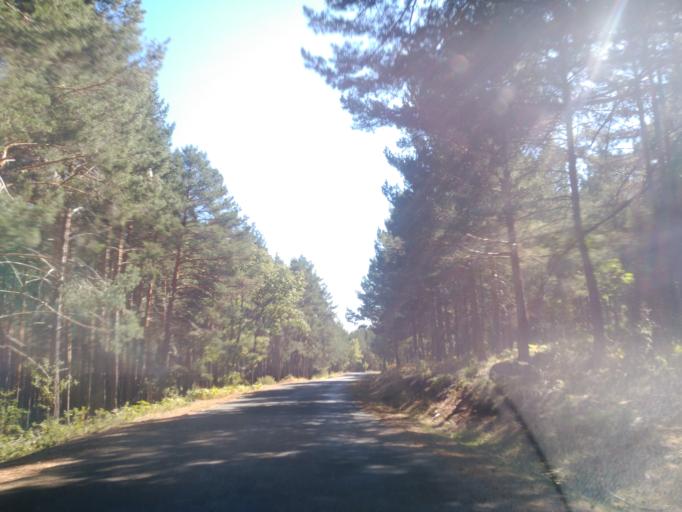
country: ES
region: Castille and Leon
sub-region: Provincia de Soria
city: Vinuesa
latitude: 41.9667
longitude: -2.7903
